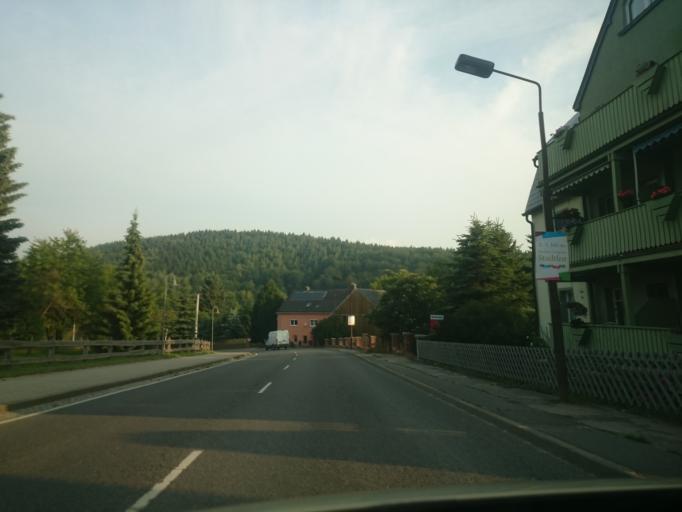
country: DE
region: Saxony
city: Pockau
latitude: 50.7124
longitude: 13.2261
